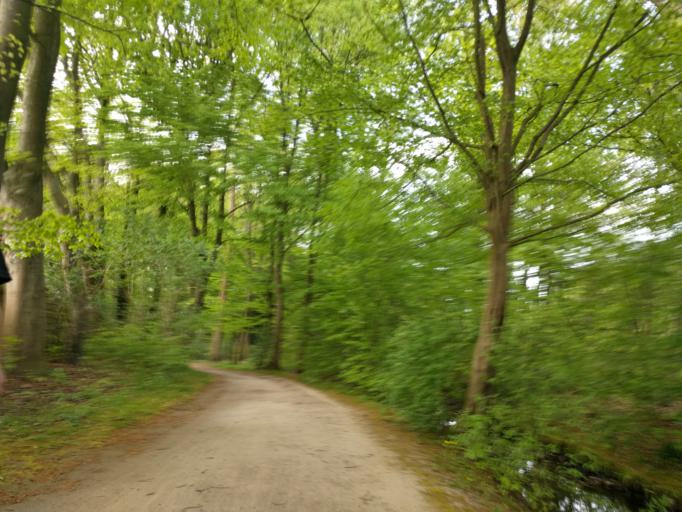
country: DE
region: North Rhine-Westphalia
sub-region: Regierungsbezirk Detmold
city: Bielefeld
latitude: 52.0489
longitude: 8.5331
